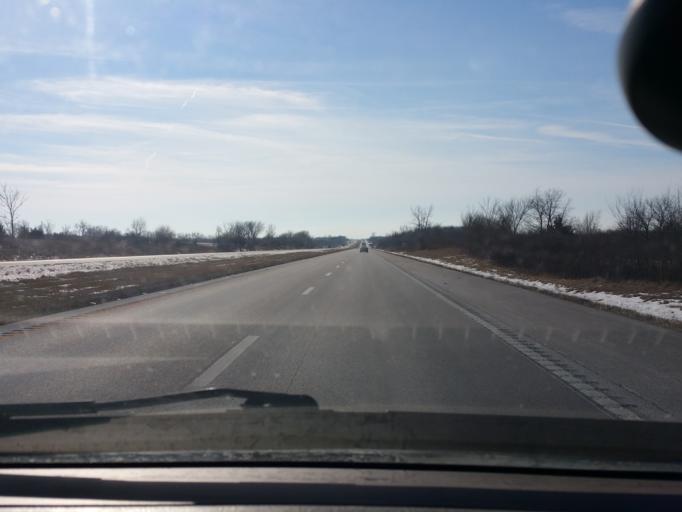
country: US
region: Missouri
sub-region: Clinton County
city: Cameron
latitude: 39.8291
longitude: -94.1876
